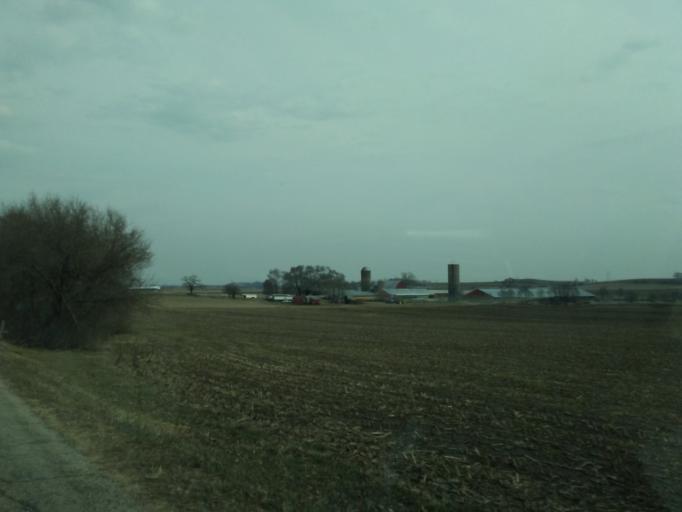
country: US
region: Wisconsin
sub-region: Dane County
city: Middleton
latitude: 43.1268
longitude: -89.4915
